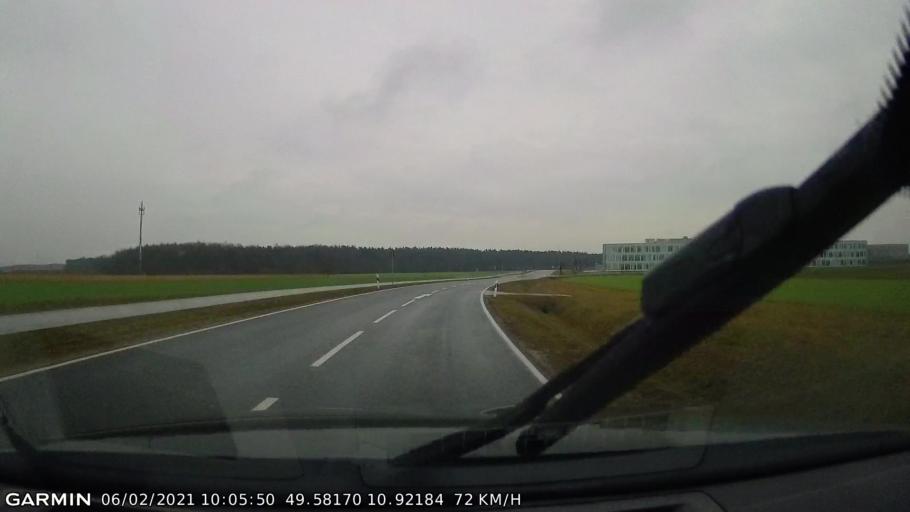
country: DE
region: Bavaria
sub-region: Regierungsbezirk Mittelfranken
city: Herzogenaurach
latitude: 49.5816
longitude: 10.9210
